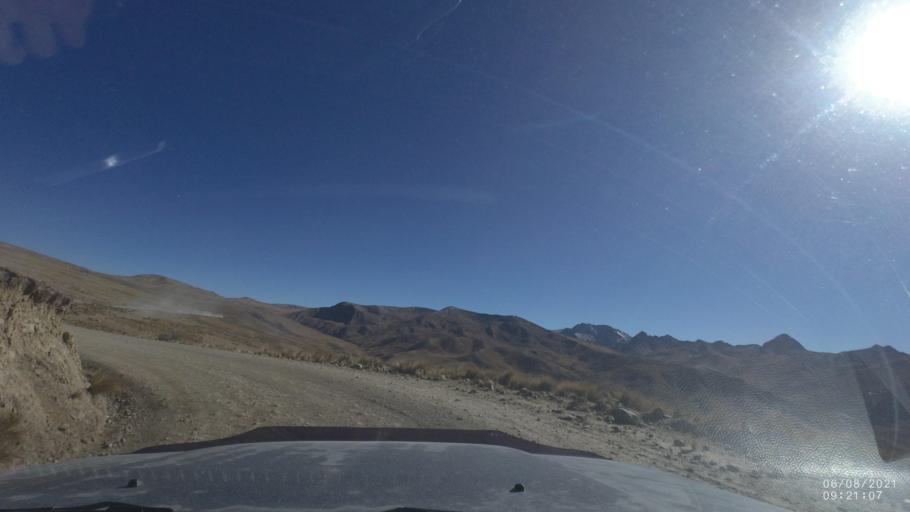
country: BO
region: Cochabamba
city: Colchani
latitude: -17.0232
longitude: -66.5427
